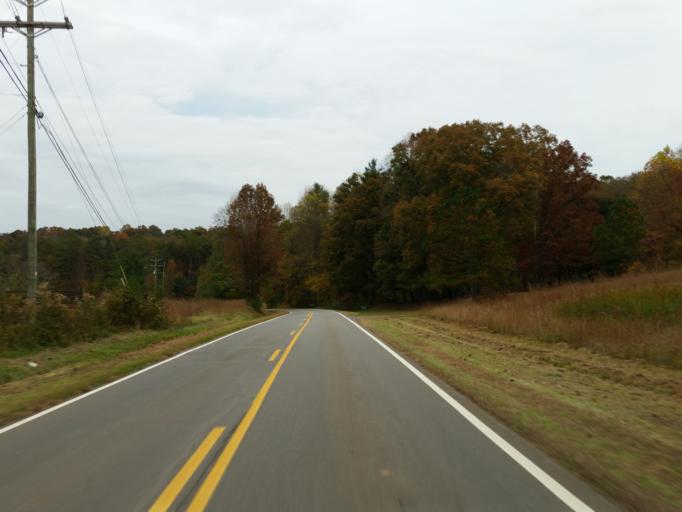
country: US
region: Georgia
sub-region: Gilmer County
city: Ellijay
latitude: 34.6541
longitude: -84.3818
